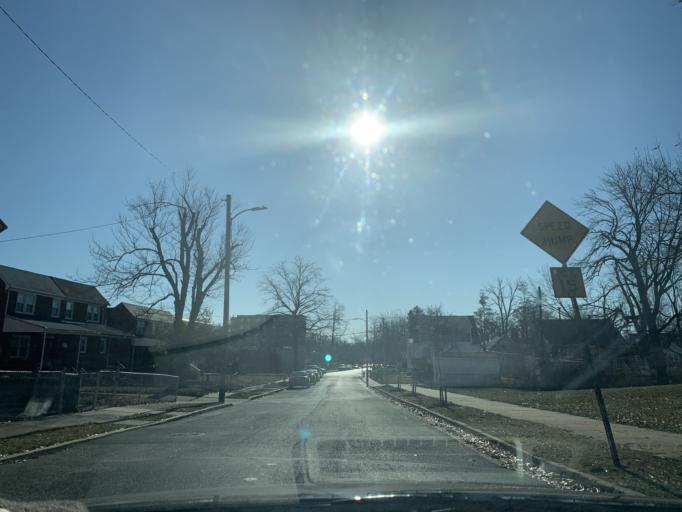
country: US
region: Maryland
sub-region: Baltimore County
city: Lochearn
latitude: 39.3363
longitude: -76.6772
